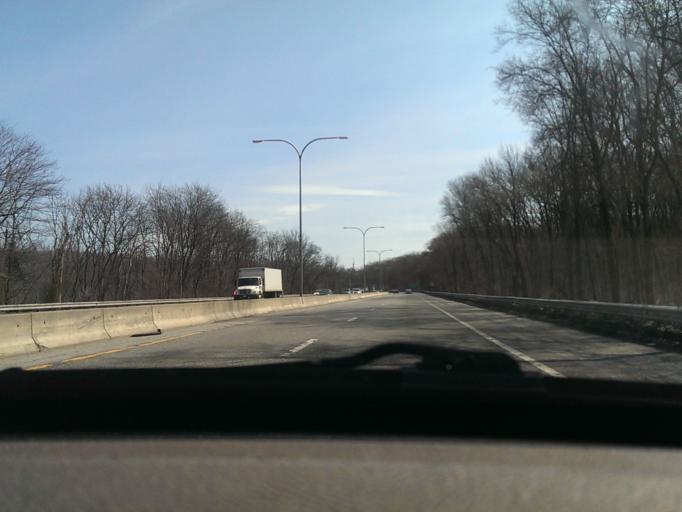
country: US
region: Rhode Island
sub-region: Providence County
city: North Providence
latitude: 41.8998
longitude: -71.4461
